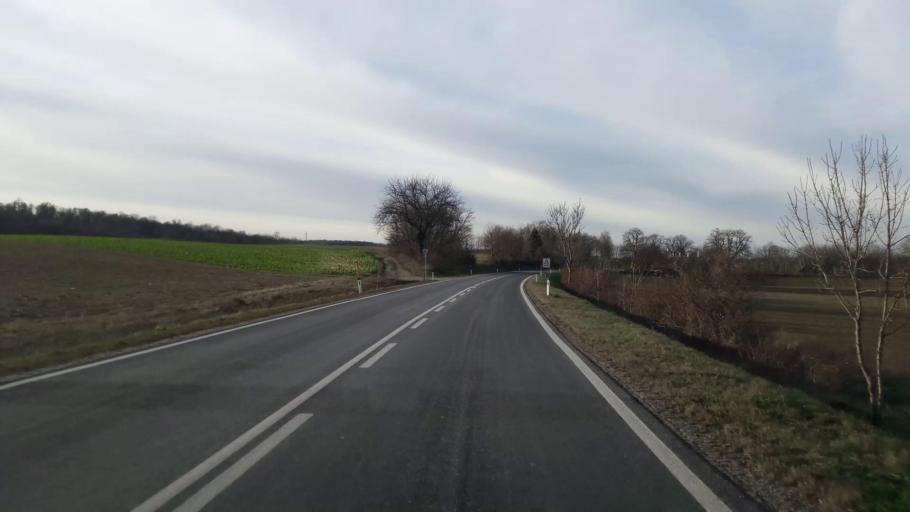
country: AT
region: Lower Austria
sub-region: Politischer Bezirk Ganserndorf
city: Gross-Schweinbarth
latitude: 48.4267
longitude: 16.6185
